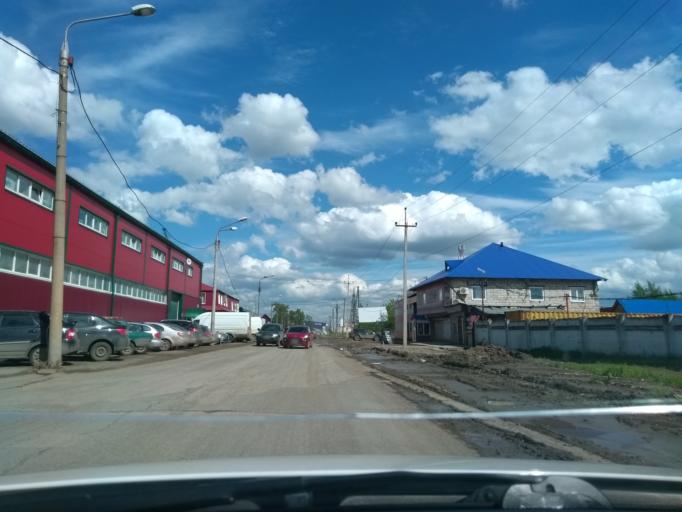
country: RU
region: Perm
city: Kondratovo
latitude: 58.0084
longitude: 56.0959
